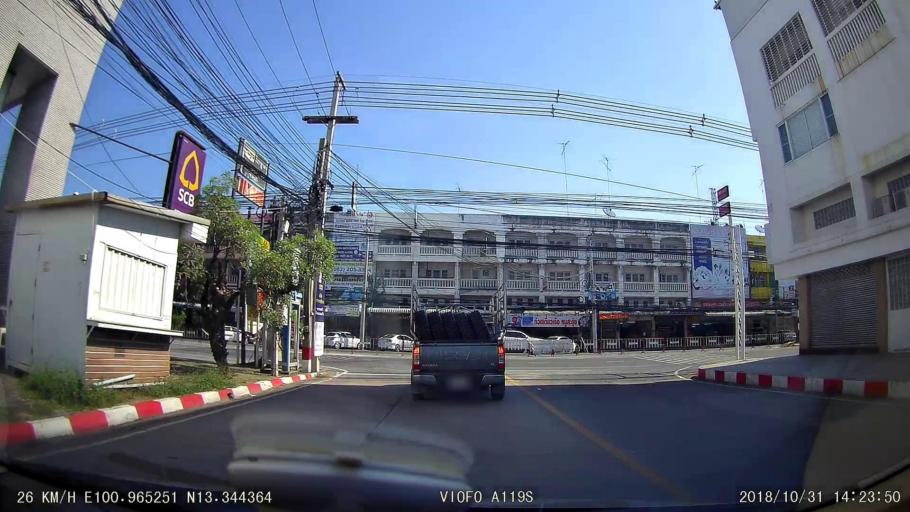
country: TH
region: Chon Buri
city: Chon Buri
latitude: 13.3443
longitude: 100.9653
